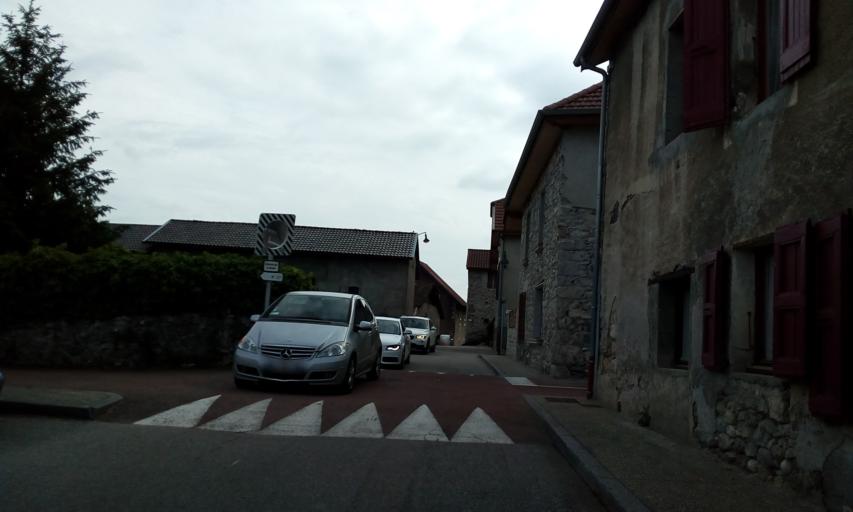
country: FR
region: Rhone-Alpes
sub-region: Departement de l'Isere
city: Saint-Vincent-de-Mercuze
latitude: 45.4000
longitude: 5.9636
